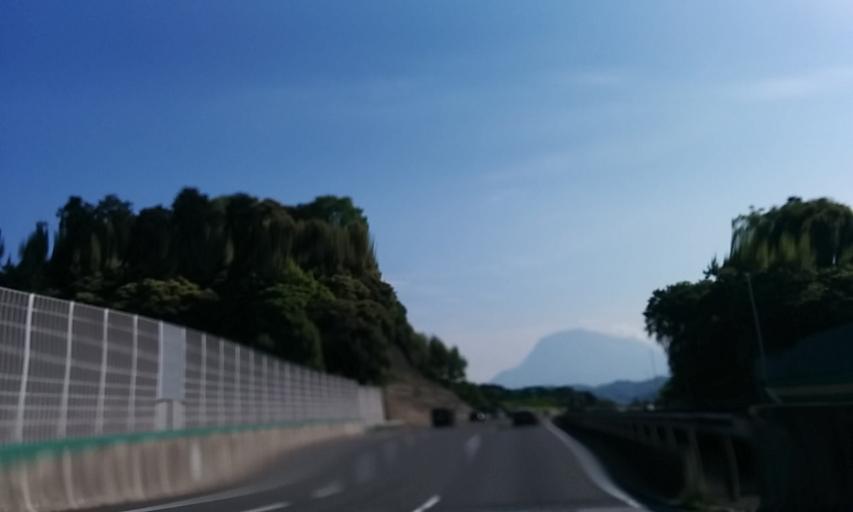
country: JP
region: Shiga Prefecture
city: Nagahama
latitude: 35.3129
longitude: 136.3148
